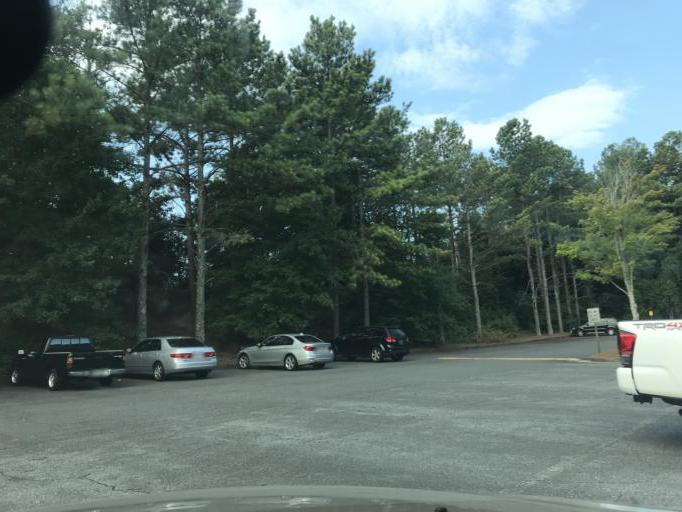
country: US
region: Georgia
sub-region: Fulton County
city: Johns Creek
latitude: 34.0657
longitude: -84.1548
